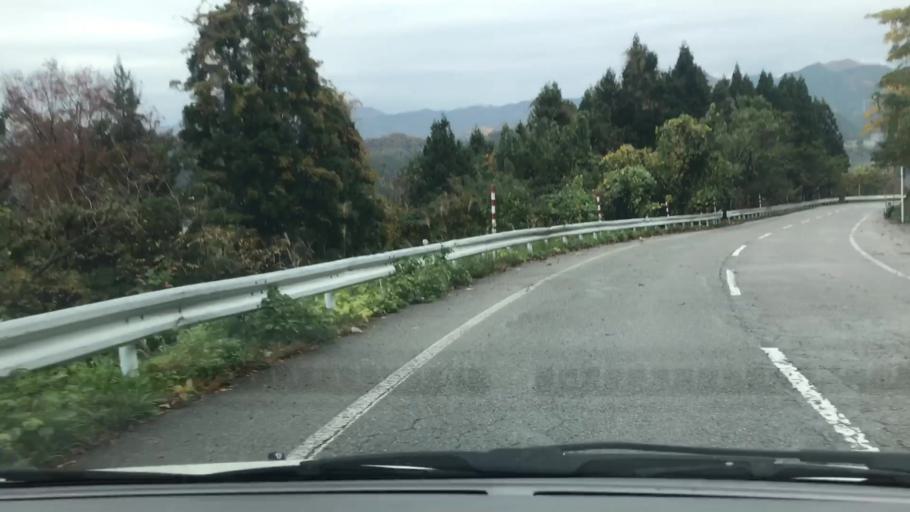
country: JP
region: Toyama
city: Kamiichi
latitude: 36.5946
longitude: 137.3139
